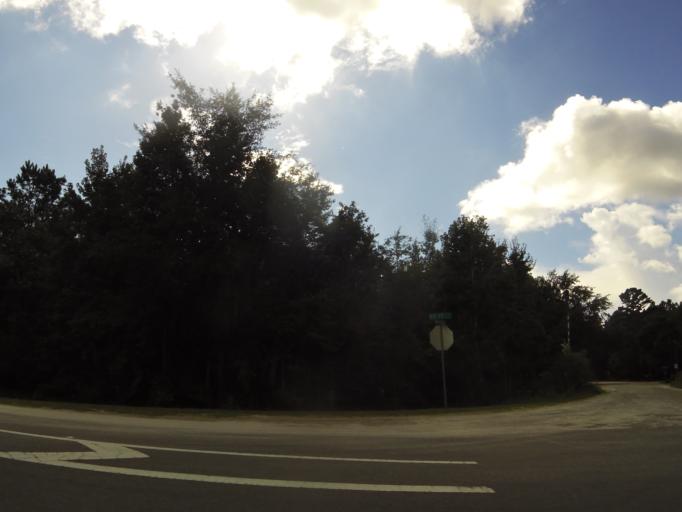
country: US
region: Georgia
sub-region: Camden County
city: Kingsland
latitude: 30.7341
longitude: -81.6883
